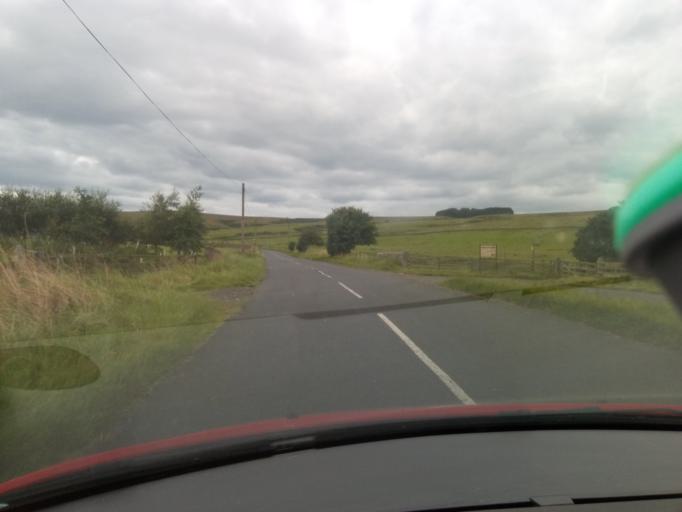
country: GB
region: England
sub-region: Northumberland
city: Corsenside
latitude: 55.1703
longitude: -2.1918
